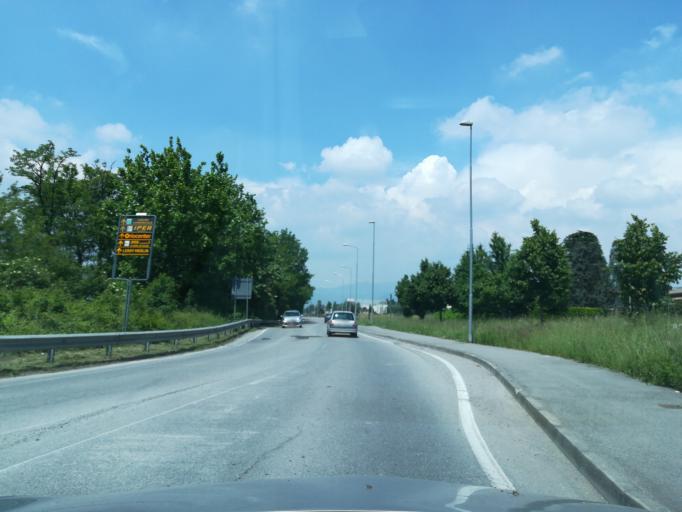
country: IT
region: Lombardy
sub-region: Provincia di Bergamo
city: Grassobbio
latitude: 45.6605
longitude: 9.7437
